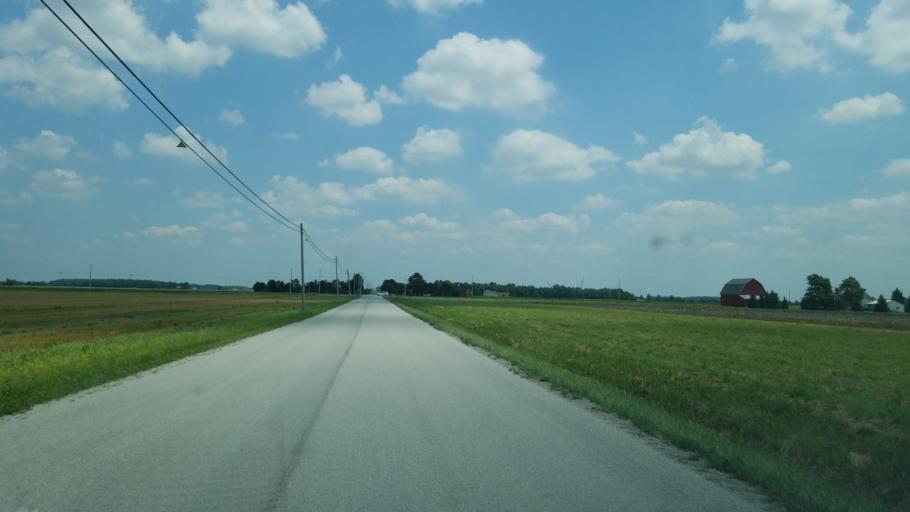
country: US
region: Ohio
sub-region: Wood County
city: North Baltimore
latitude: 41.2399
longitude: -83.5959
